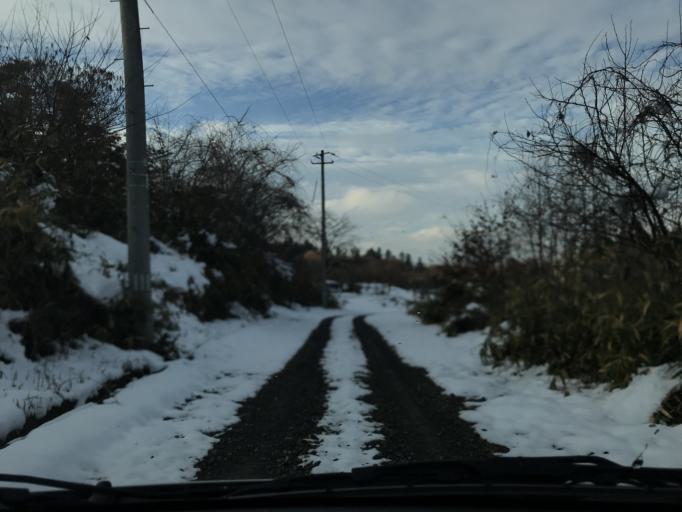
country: JP
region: Iwate
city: Mizusawa
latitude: 39.0384
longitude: 141.1023
